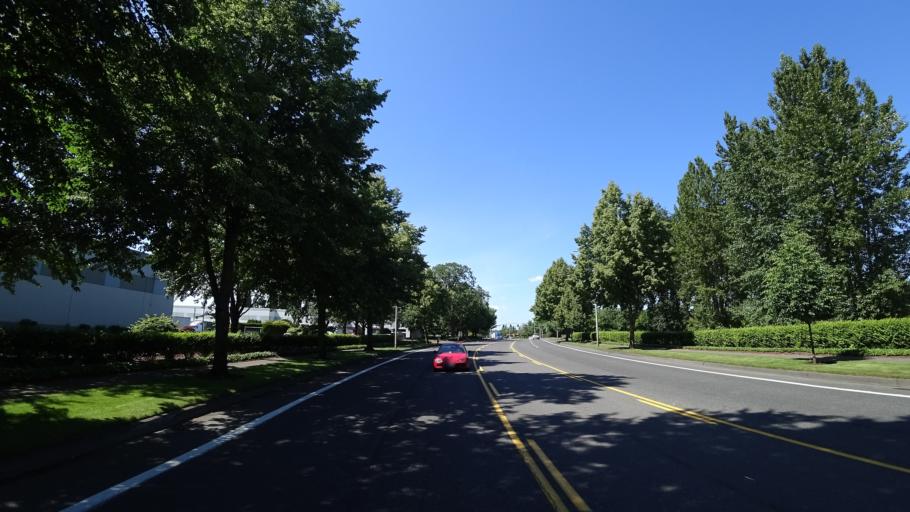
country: US
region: Oregon
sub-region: Multnomah County
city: Lents
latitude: 45.5730
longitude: -122.5746
